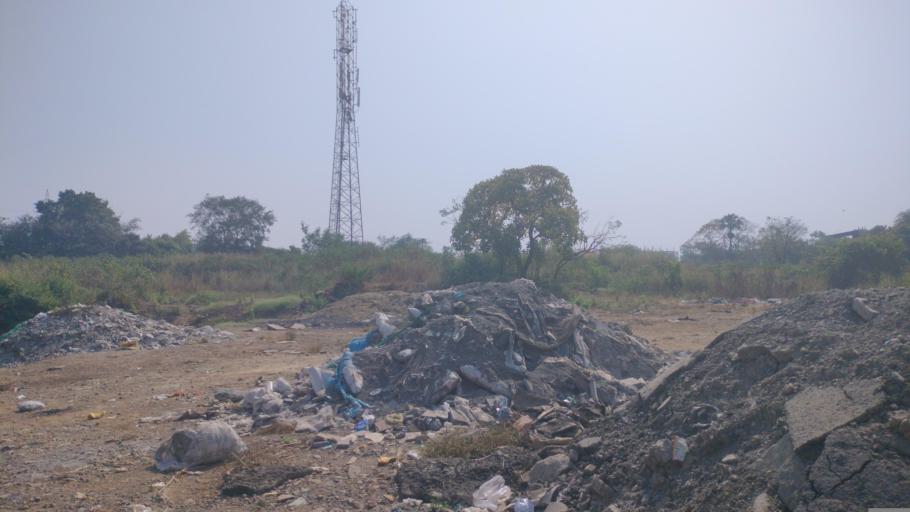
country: IN
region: Maharashtra
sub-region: Thane
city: Bhayandar
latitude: 19.3660
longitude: 72.9065
